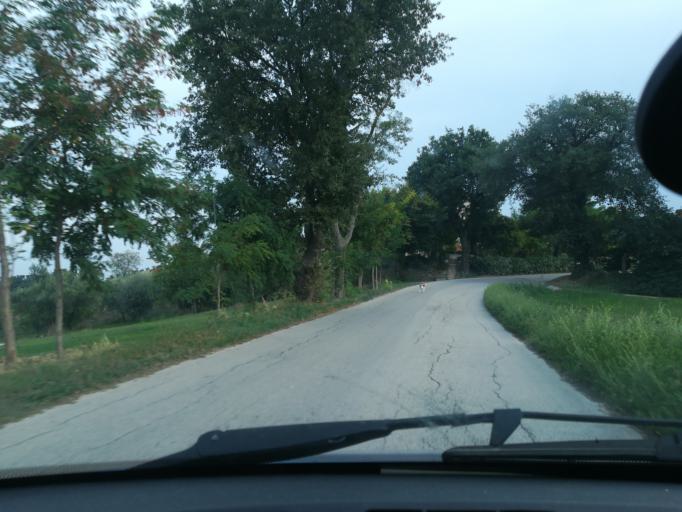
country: IT
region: The Marches
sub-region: Provincia di Macerata
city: Piediripa
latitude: 43.3018
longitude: 13.4797
